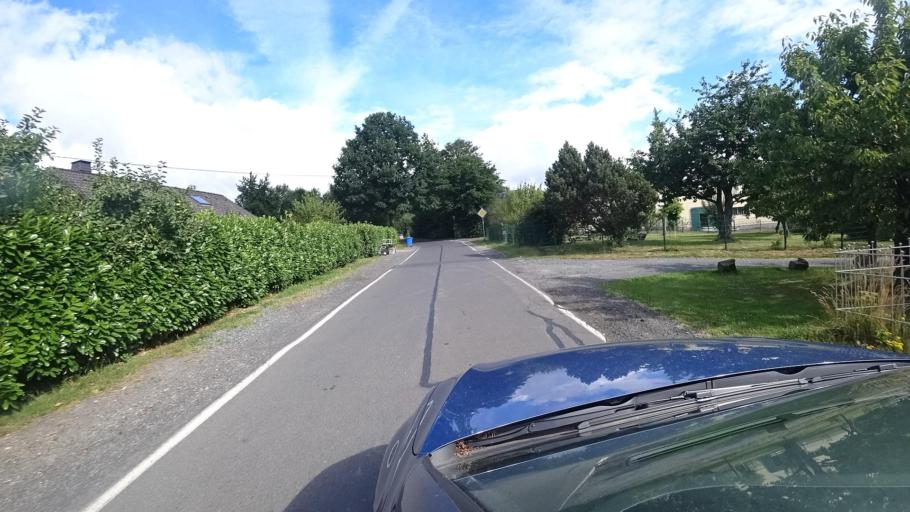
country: DE
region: Rheinland-Pfalz
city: Ziegenhain
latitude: 50.6753
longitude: 7.5260
